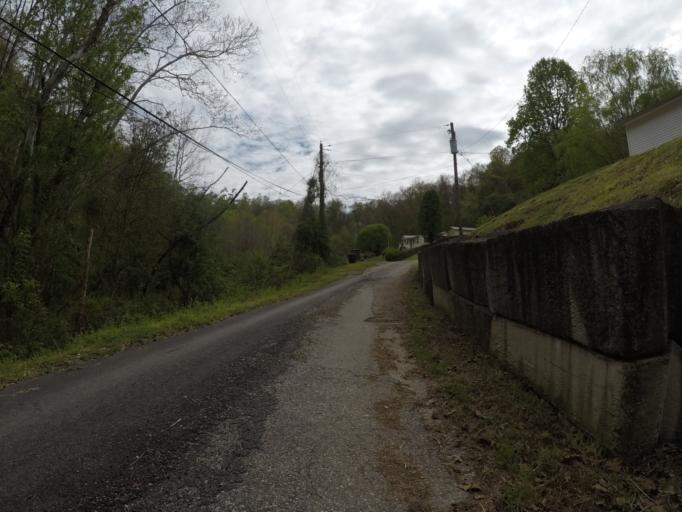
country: US
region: West Virginia
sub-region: Cabell County
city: Huntington
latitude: 38.3899
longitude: -82.4857
